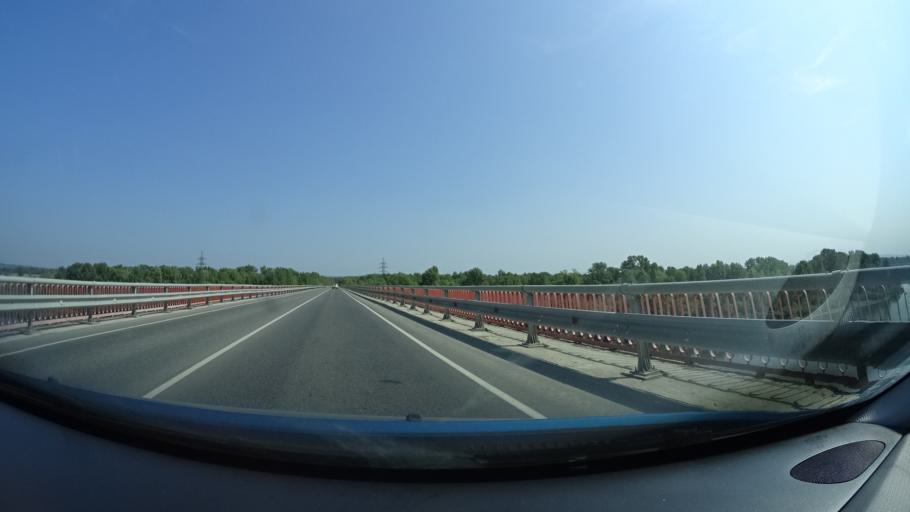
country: RU
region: Bashkortostan
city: Ulukulevo
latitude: 54.4494
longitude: 56.4605
